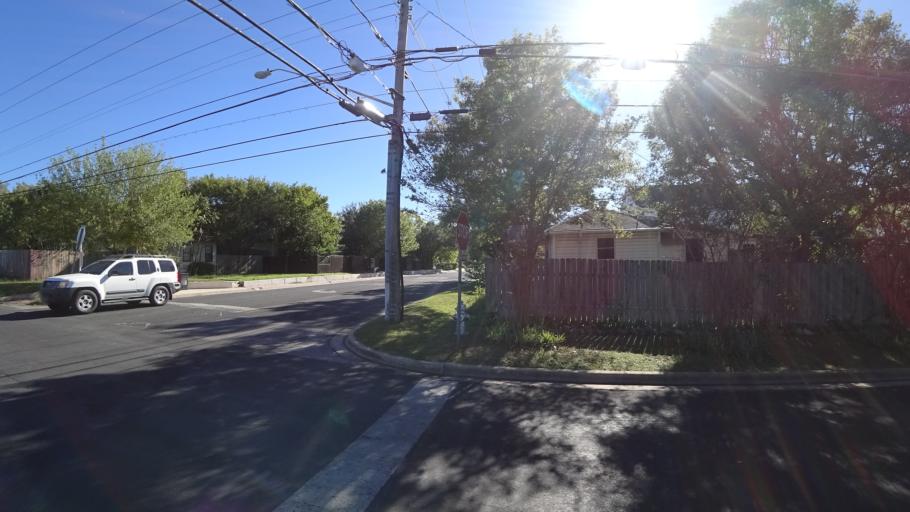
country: US
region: Texas
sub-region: Travis County
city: Austin
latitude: 30.3264
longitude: -97.7345
